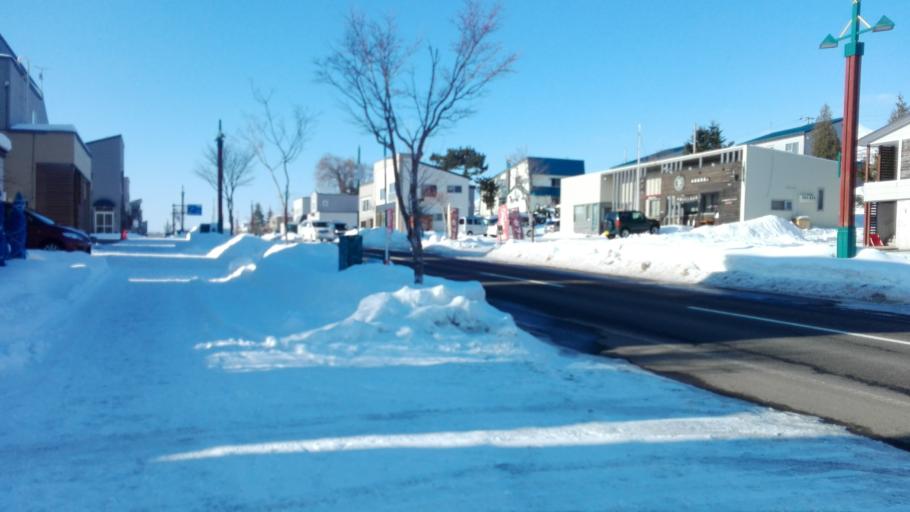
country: JP
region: Hokkaido
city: Niseko Town
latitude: 42.8030
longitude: 140.6888
